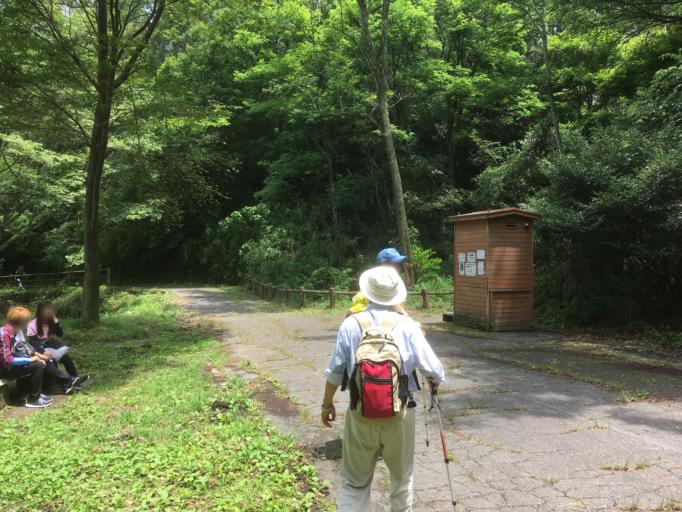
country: JP
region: Nara
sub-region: Ikoma-shi
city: Ikoma
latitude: 34.6913
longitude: 135.6702
